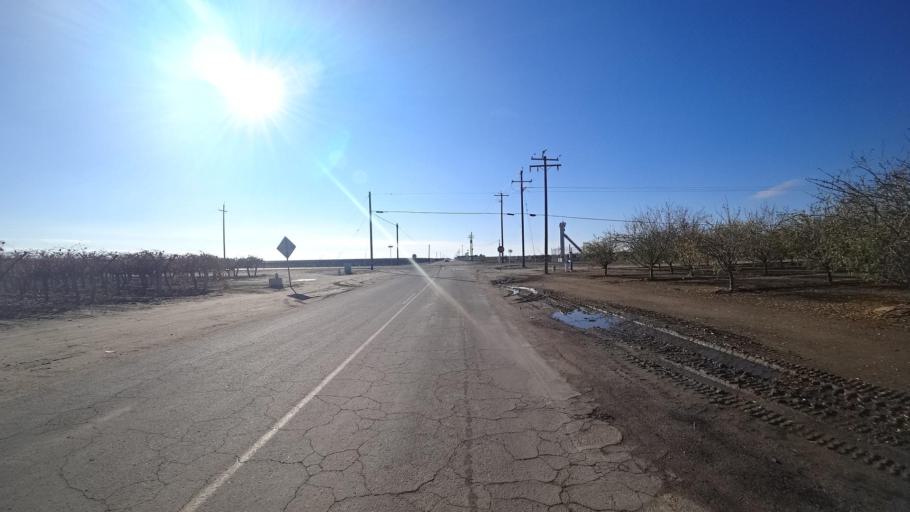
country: US
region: California
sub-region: Kern County
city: Delano
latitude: 35.7184
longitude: -119.2763
